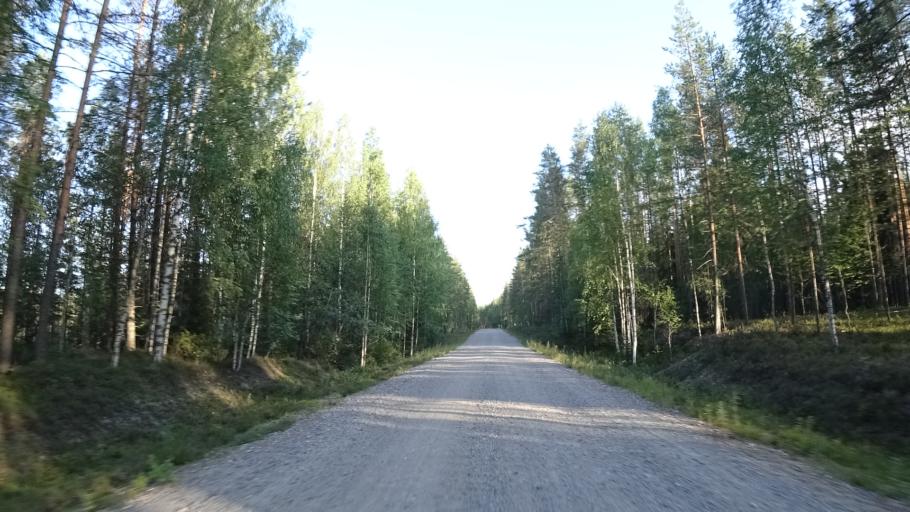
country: FI
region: North Karelia
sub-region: Joensuu
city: Ilomantsi
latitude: 63.1316
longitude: 30.7101
